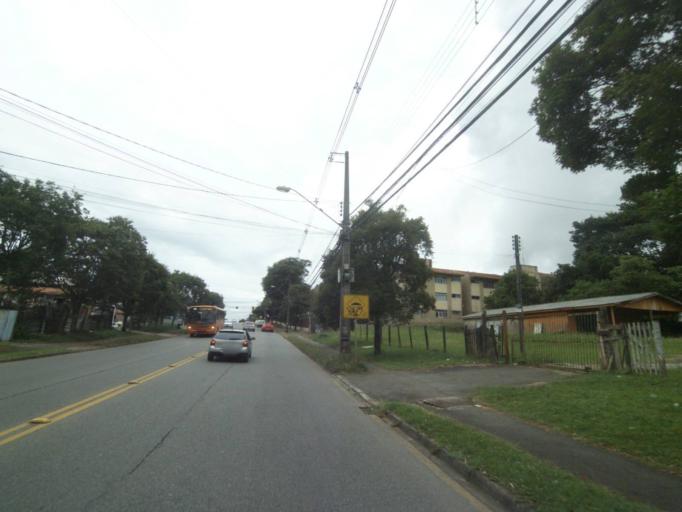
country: BR
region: Parana
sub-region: Curitiba
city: Curitiba
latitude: -25.4610
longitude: -49.3275
